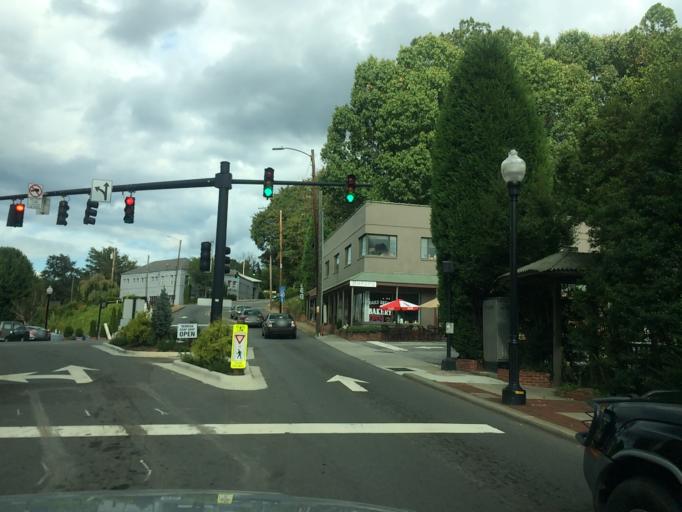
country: US
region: North Carolina
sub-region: Haywood County
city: Canton
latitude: 35.5327
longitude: -82.8377
